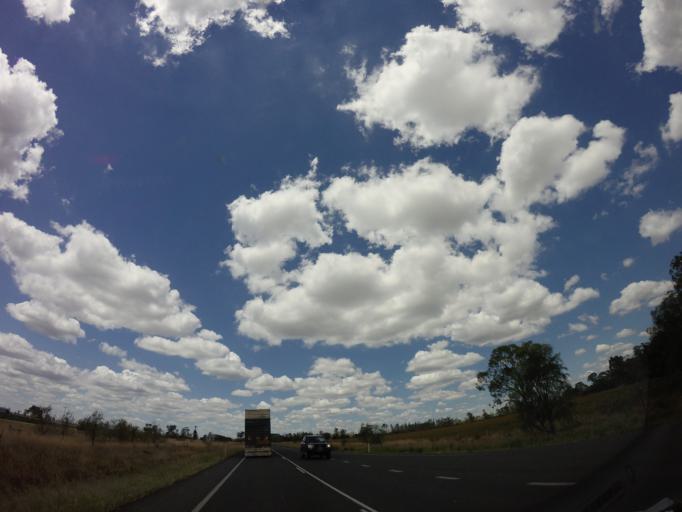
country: AU
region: Queensland
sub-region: Toowoomba
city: Oakey
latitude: -27.8316
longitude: 151.3474
